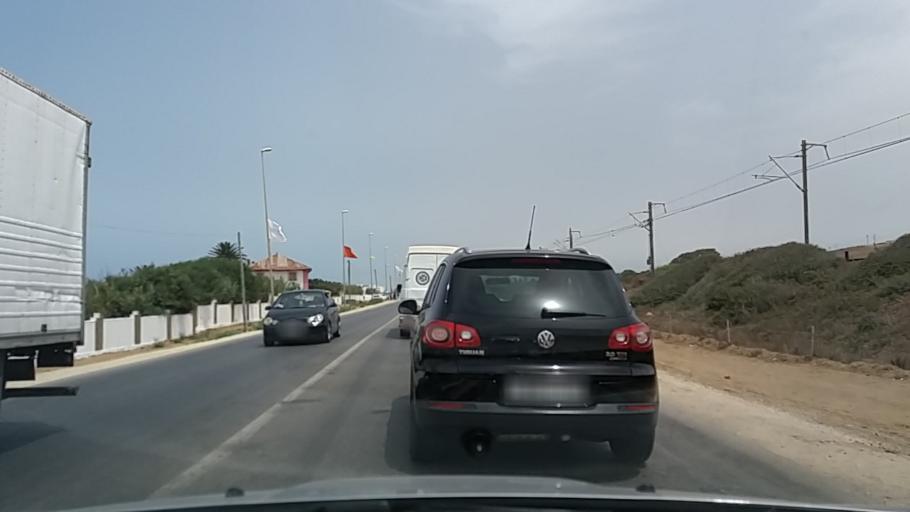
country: MA
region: Tanger-Tetouan
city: Asilah
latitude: 35.4788
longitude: -6.0255
